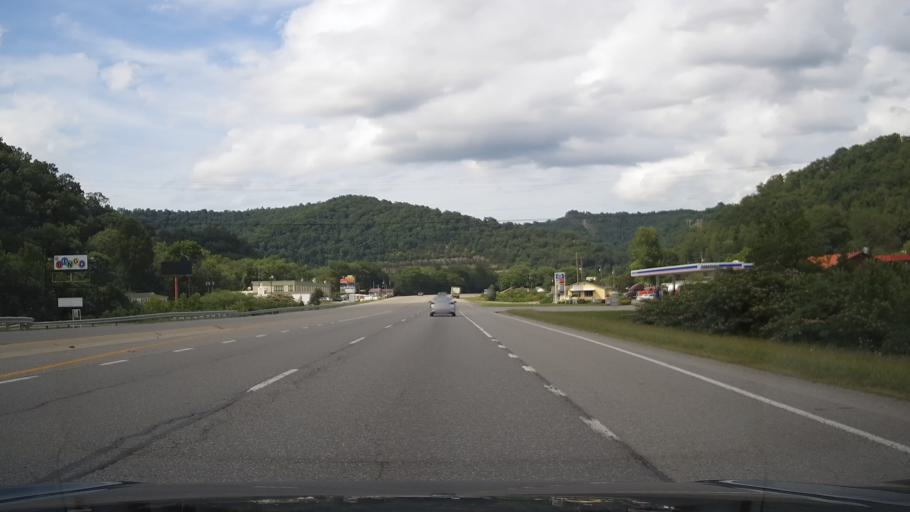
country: US
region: Kentucky
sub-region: Pike County
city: Coal Run Village
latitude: 37.5628
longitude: -82.6454
